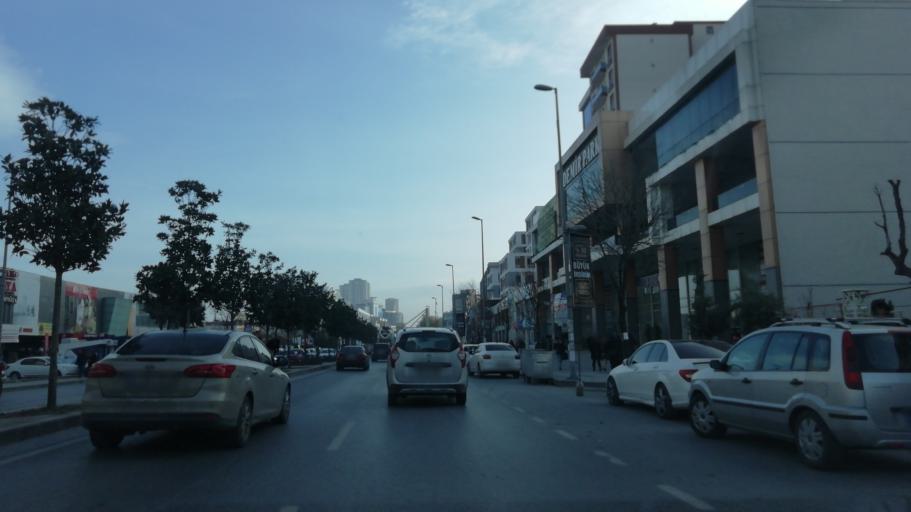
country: TR
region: Istanbul
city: Esenyurt
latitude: 41.0413
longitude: 28.6767
